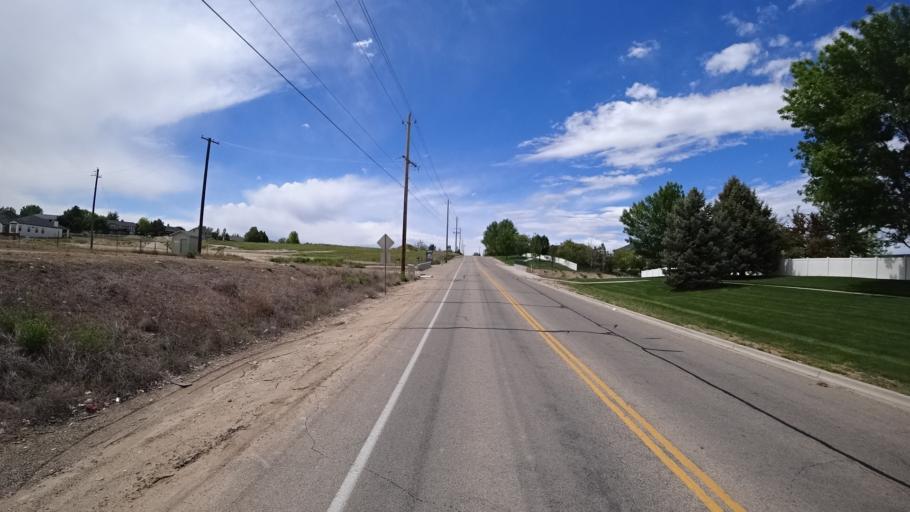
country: US
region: Idaho
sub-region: Ada County
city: Meridian
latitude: 43.5755
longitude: -116.4001
